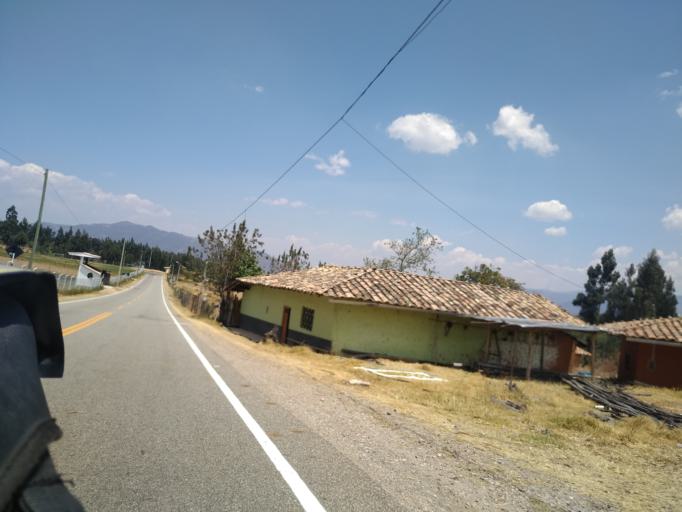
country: PE
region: Cajamarca
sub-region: San Marcos
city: San Marcos
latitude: -7.2884
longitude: -78.2064
